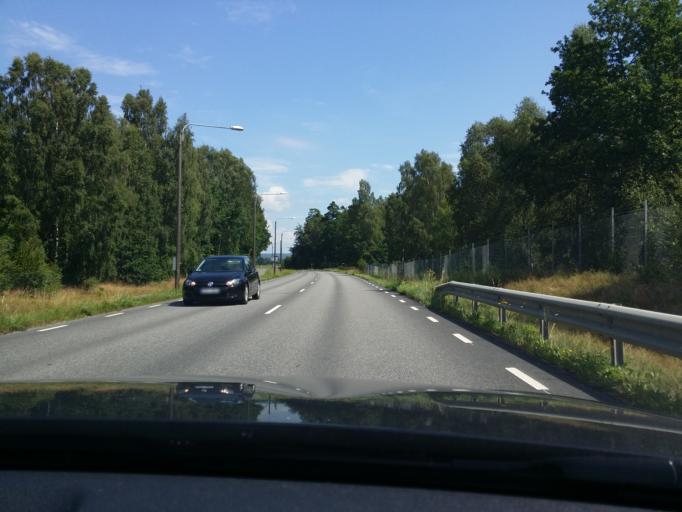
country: SE
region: Skane
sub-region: Bromolla Kommun
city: Bromoella
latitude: 56.0453
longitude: 14.4769
